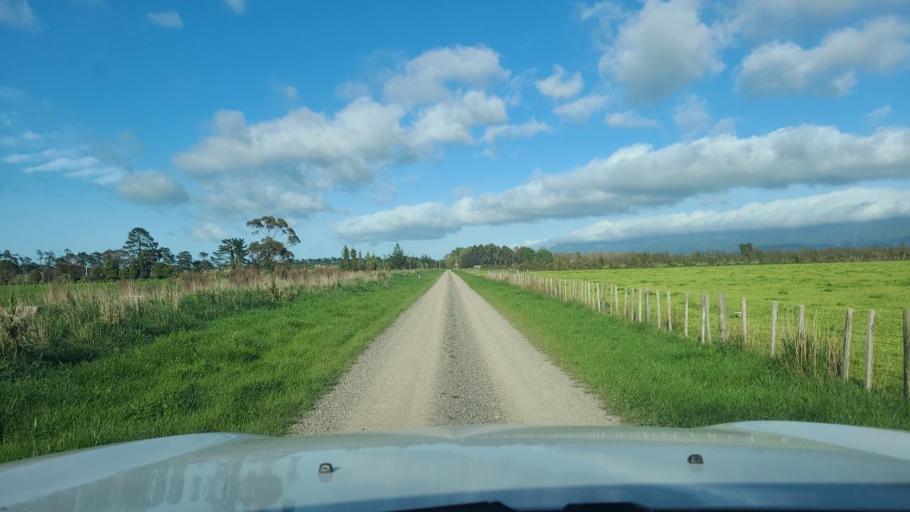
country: NZ
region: Wellington
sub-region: Upper Hutt City
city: Upper Hutt
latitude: -41.2985
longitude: 175.2668
